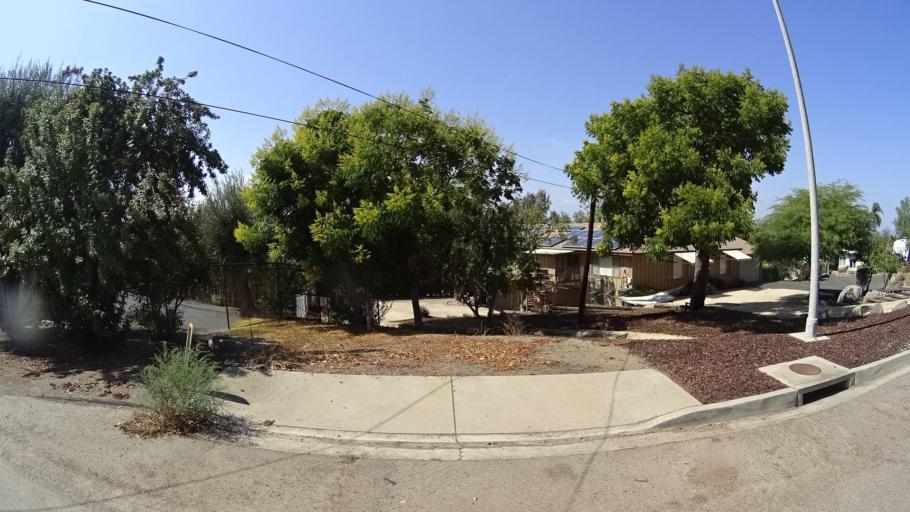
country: US
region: California
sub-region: San Diego County
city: Granite Hills
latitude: 32.7810
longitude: -116.9177
